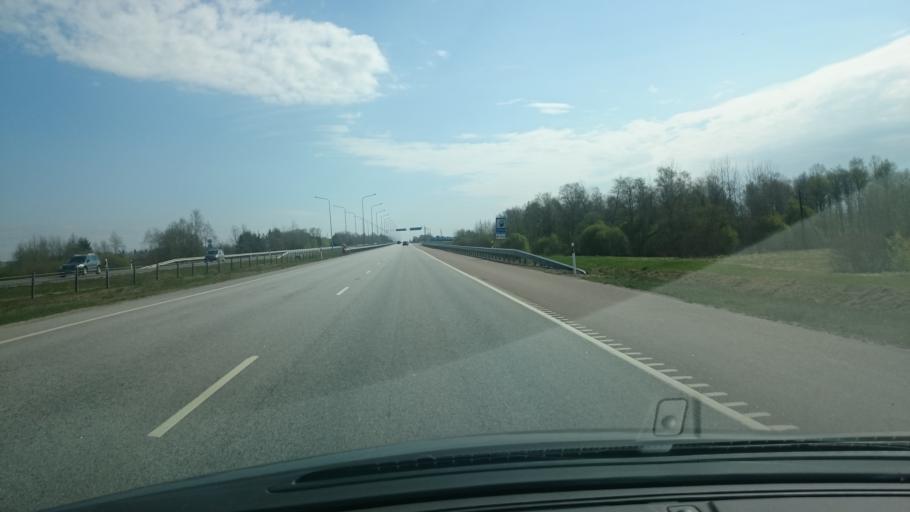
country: EE
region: Harju
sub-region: Kuusalu vald
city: Kuusalu
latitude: 59.4444
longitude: 25.3625
